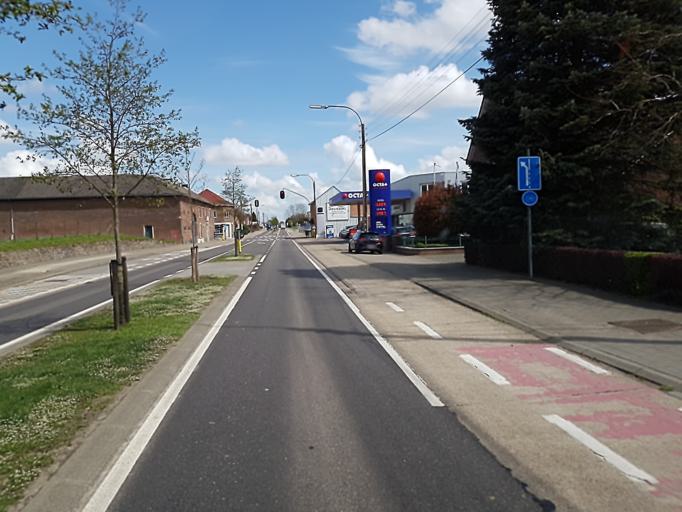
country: BE
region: Flanders
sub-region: Provincie Limburg
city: Riemst
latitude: 50.8036
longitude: 5.5726
